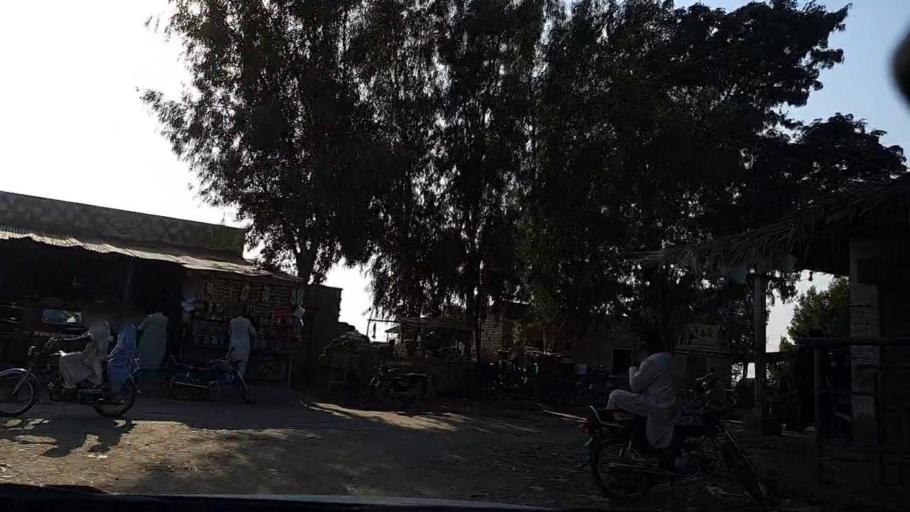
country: PK
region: Sindh
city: Tando Ghulam Ali
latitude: 25.2240
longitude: 68.9441
